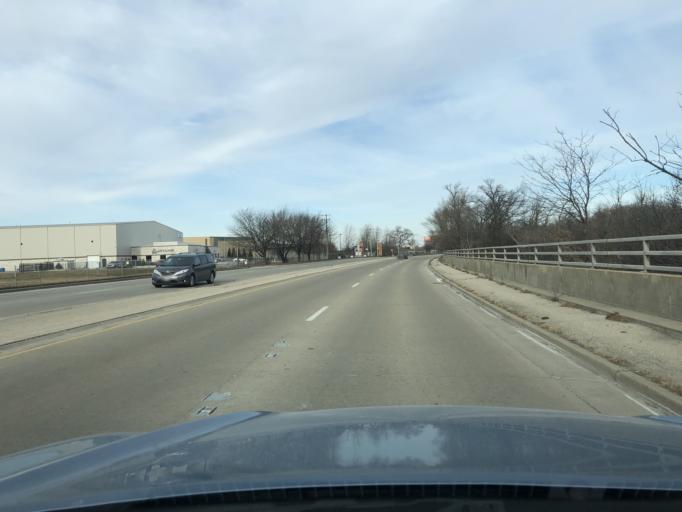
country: US
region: Illinois
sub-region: Cook County
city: Wheeling
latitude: 42.1152
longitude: -87.8936
